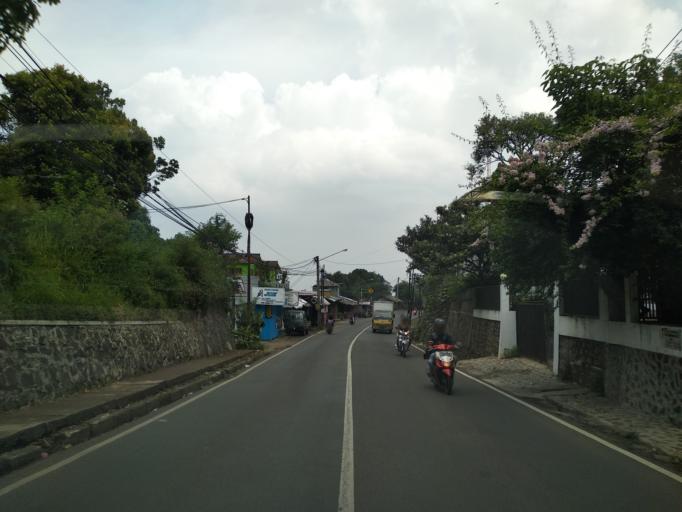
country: ID
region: West Java
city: Lembang
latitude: -6.8245
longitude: 107.6101
